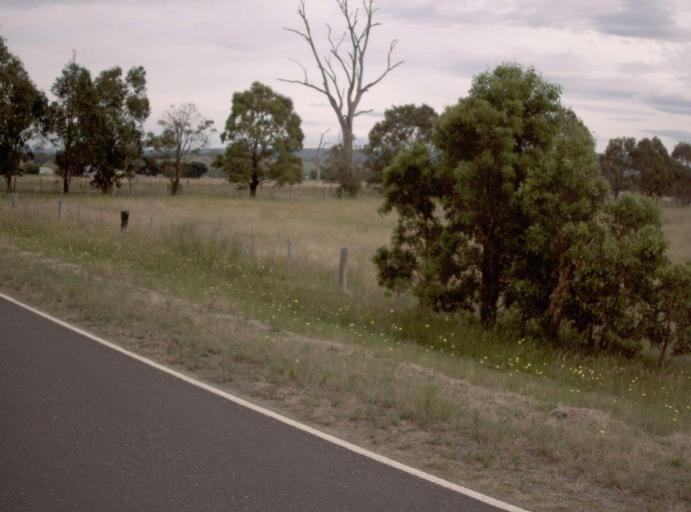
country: AU
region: Victoria
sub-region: East Gippsland
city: Bairnsdale
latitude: -37.8326
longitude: 147.5567
